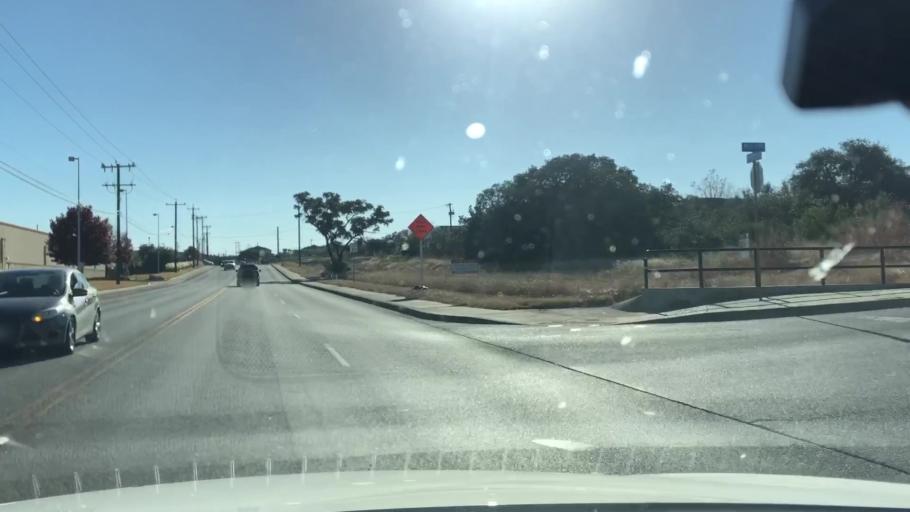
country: US
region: Texas
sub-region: Bexar County
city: Helotes
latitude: 29.4907
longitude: -98.7124
